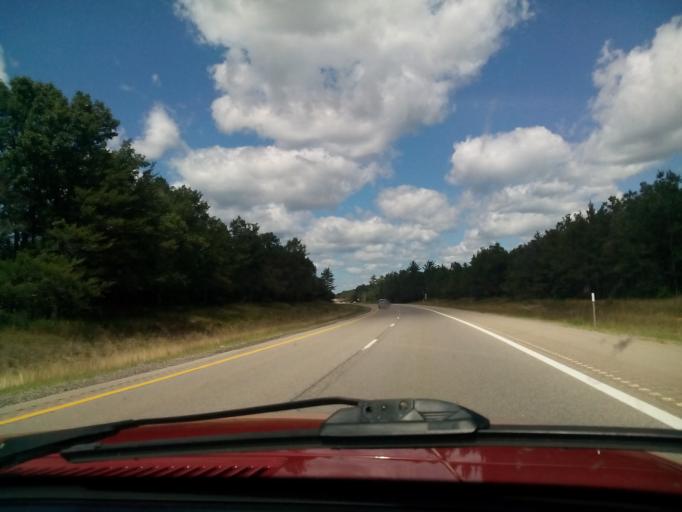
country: US
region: Michigan
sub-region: Crawford County
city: Grayling
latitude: 44.6598
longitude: -84.6977
